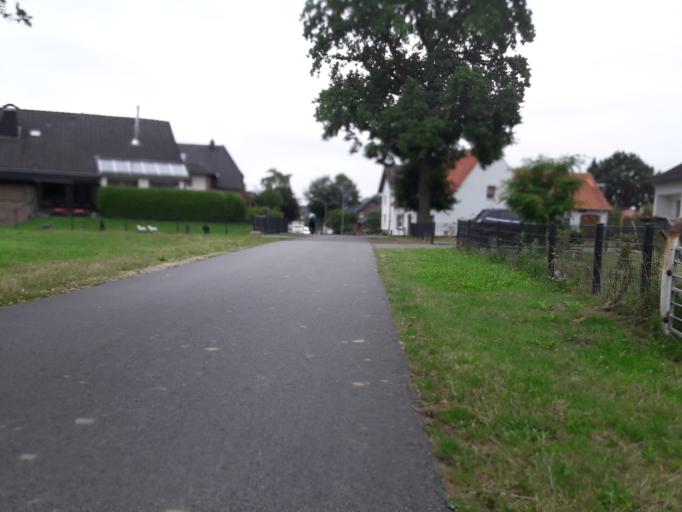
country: DE
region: North Rhine-Westphalia
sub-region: Regierungsbezirk Detmold
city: Salzkotten
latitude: 51.7195
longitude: 8.6322
